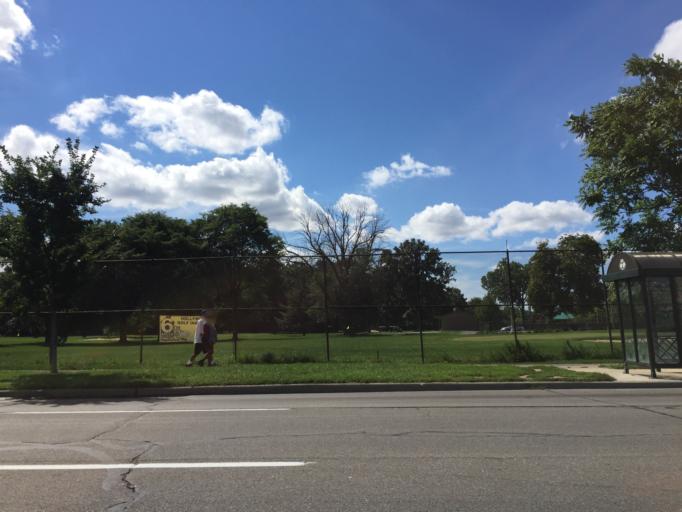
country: US
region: Michigan
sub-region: Wayne County
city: Highland Park
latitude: 42.4317
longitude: -83.1151
